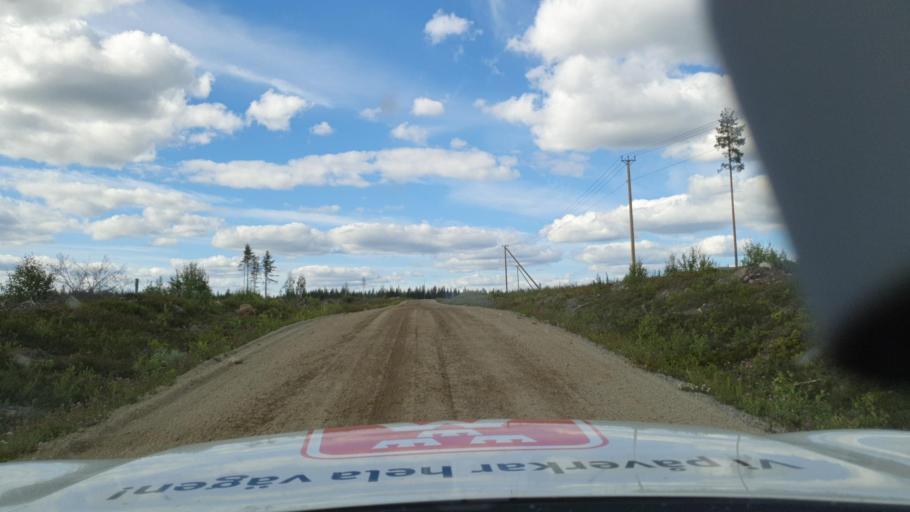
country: SE
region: Vaesterbotten
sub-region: Lycksele Kommun
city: Lycksele
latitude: 64.3020
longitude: 18.2877
